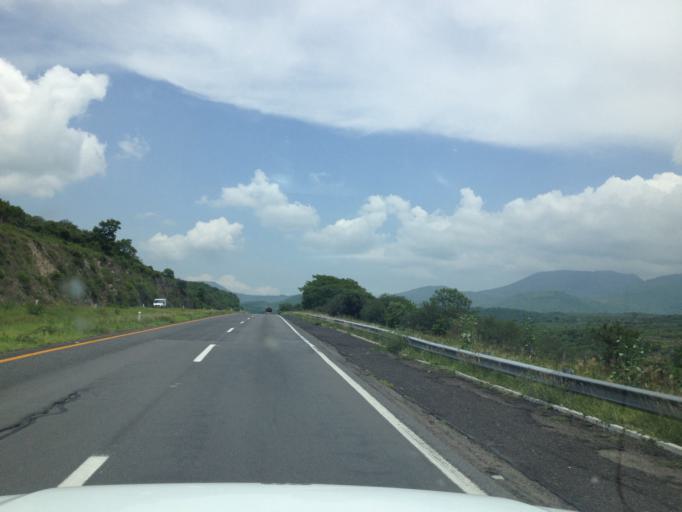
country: MX
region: Mexico
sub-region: Chapultepec
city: Chucandiro
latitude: 19.8837
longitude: -101.3403
